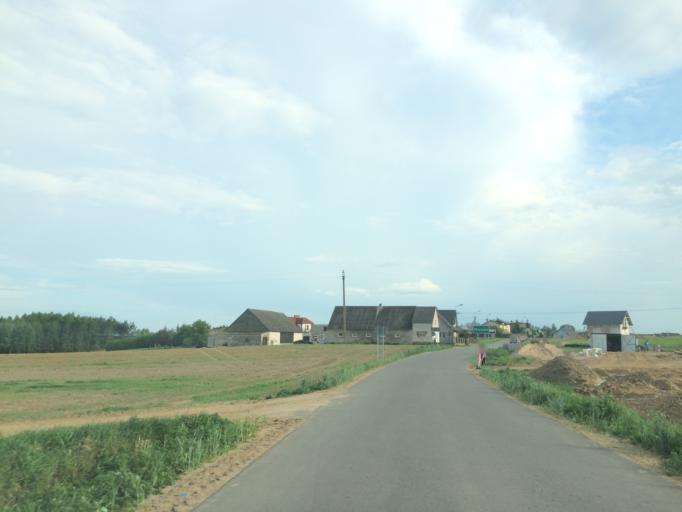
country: PL
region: Kujawsko-Pomorskie
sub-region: Powiat brodnicki
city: Brzozie
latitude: 53.3621
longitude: 19.7106
